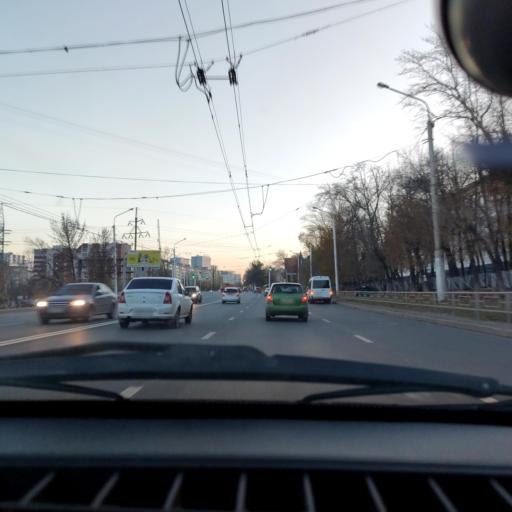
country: RU
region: Bashkortostan
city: Ufa
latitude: 54.7748
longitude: 56.0343
